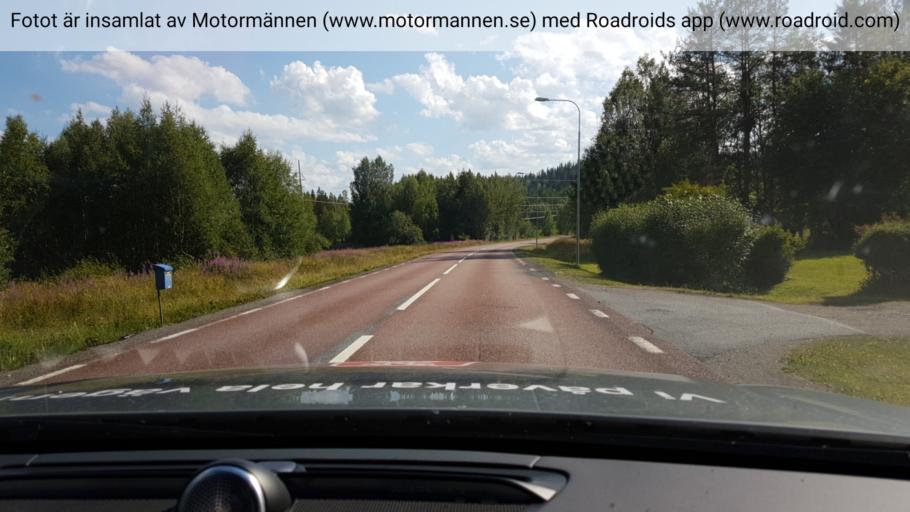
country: SE
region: Vaesterbotten
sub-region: Dorotea Kommun
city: Dorotea
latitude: 64.0413
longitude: 16.0207
